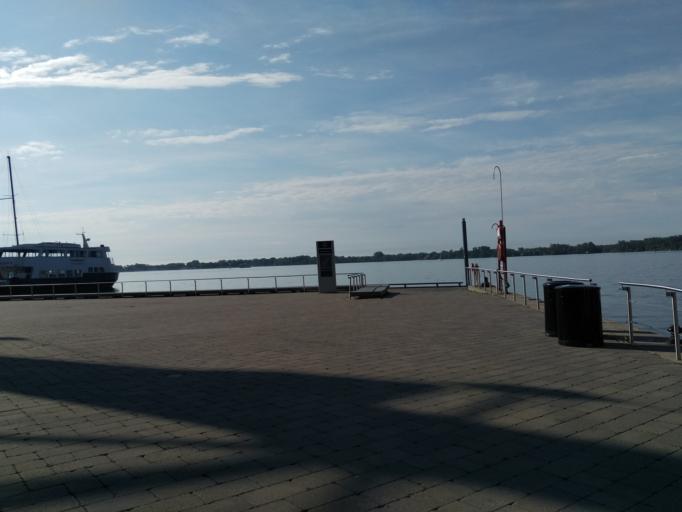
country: CA
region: Ontario
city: Toronto
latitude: 43.6379
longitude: -79.3837
